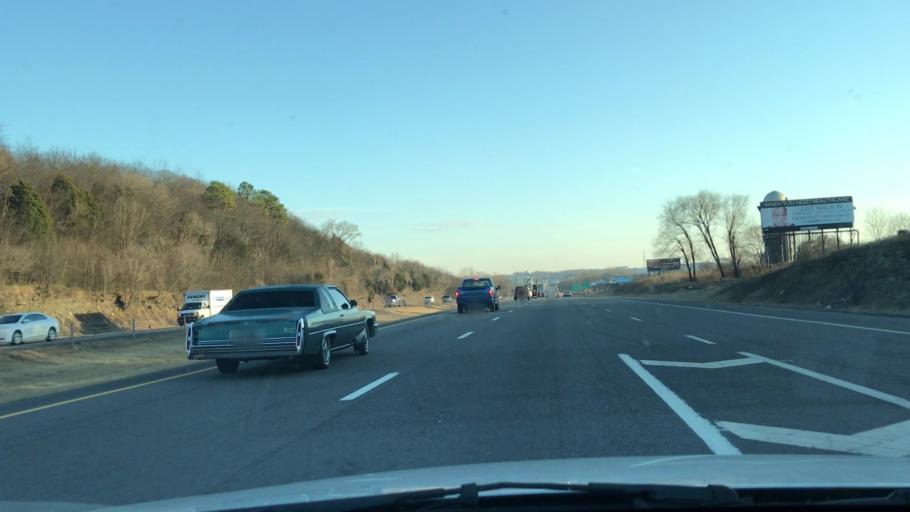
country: US
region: Tennessee
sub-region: Davidson County
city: Goodlettsville
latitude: 36.3432
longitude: -86.7147
